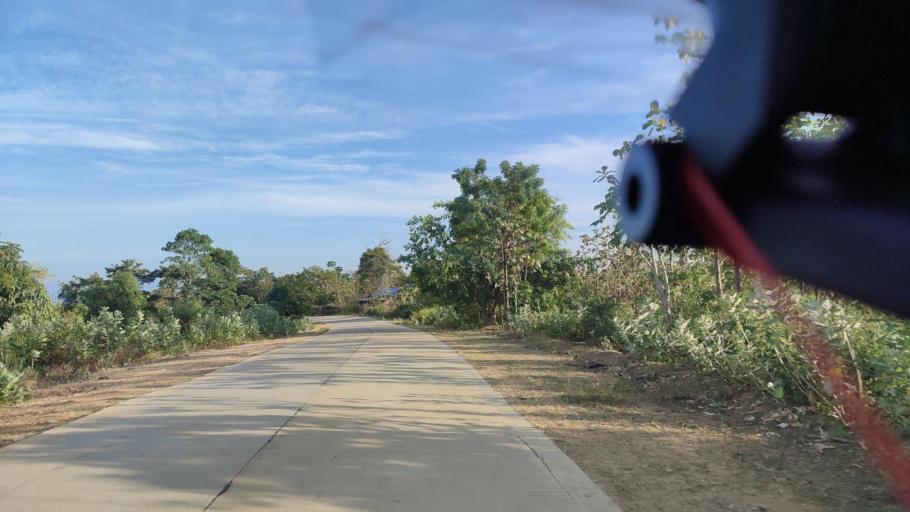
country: MM
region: Magway
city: Taungdwingyi
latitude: 20.0241
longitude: 95.8219
